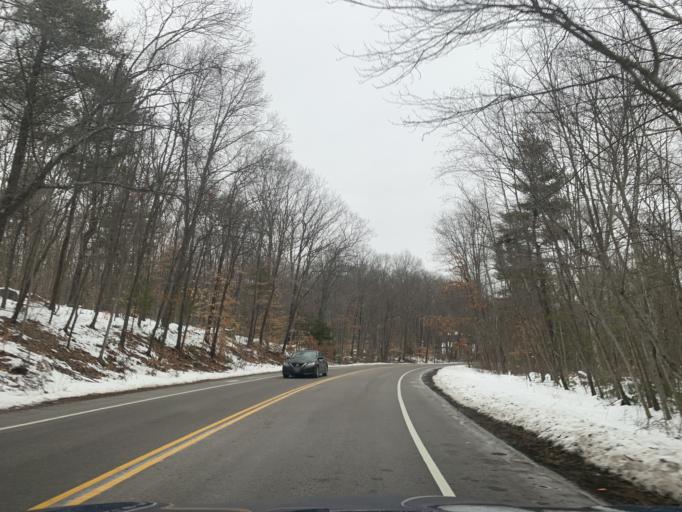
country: US
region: Massachusetts
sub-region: Norfolk County
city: Milton
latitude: 42.2307
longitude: -71.0941
